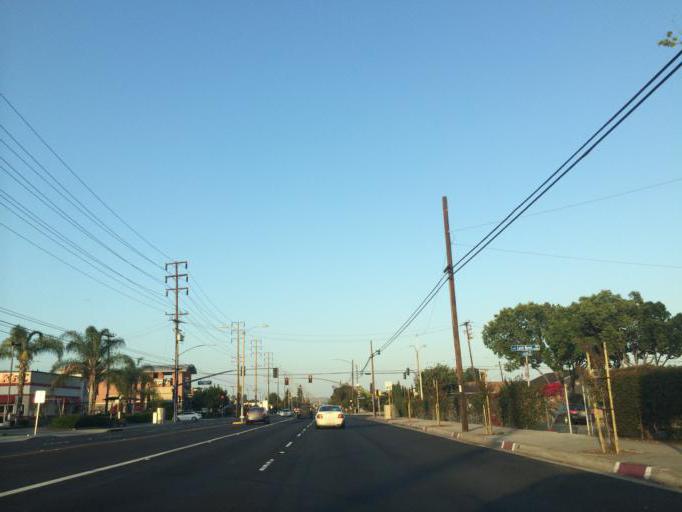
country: US
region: California
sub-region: Los Angeles County
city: Norwalk
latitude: 33.9023
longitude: -118.0565
